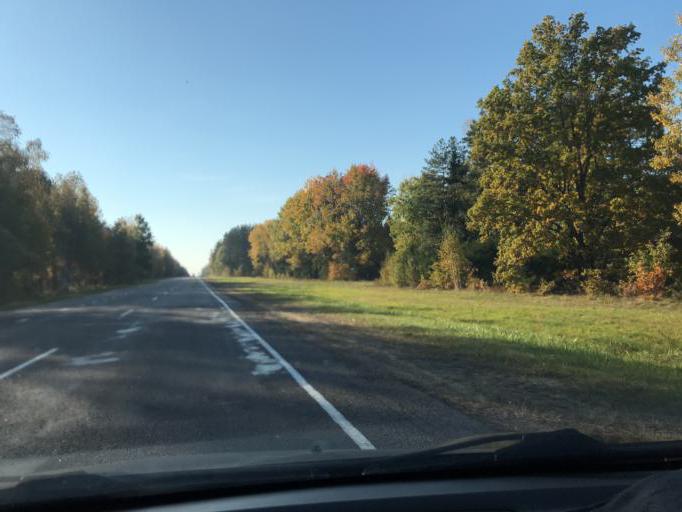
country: BY
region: Minsk
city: Staryya Darohi
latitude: 53.0461
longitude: 28.3552
